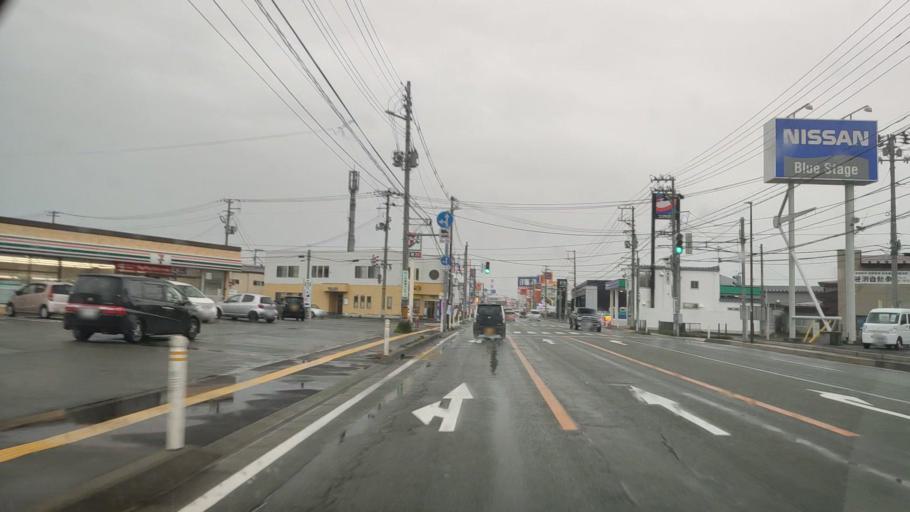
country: JP
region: Akita
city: Akita Shi
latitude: 39.7314
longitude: 140.1025
